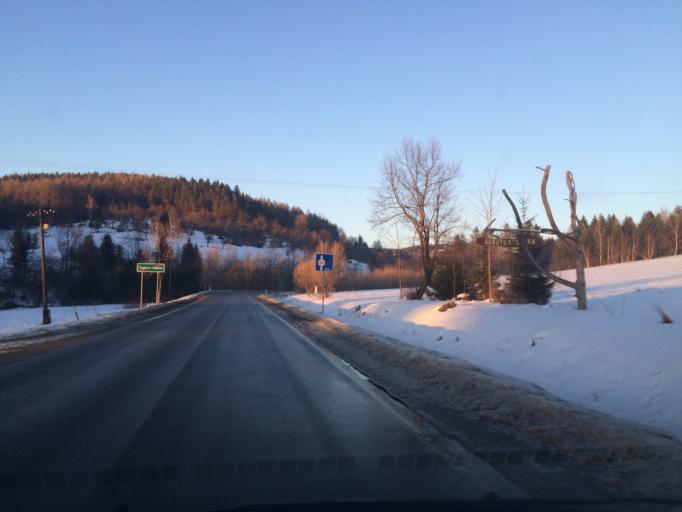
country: PL
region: Subcarpathian Voivodeship
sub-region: Powiat bieszczadzki
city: Czarna
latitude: 49.3399
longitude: 22.6739
